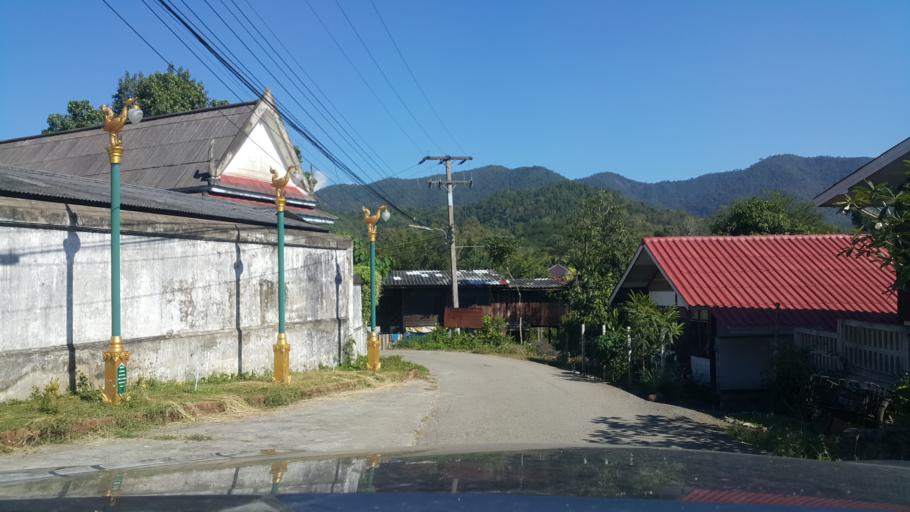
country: TH
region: Chiang Mai
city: Mae On
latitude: 18.7885
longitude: 99.2578
